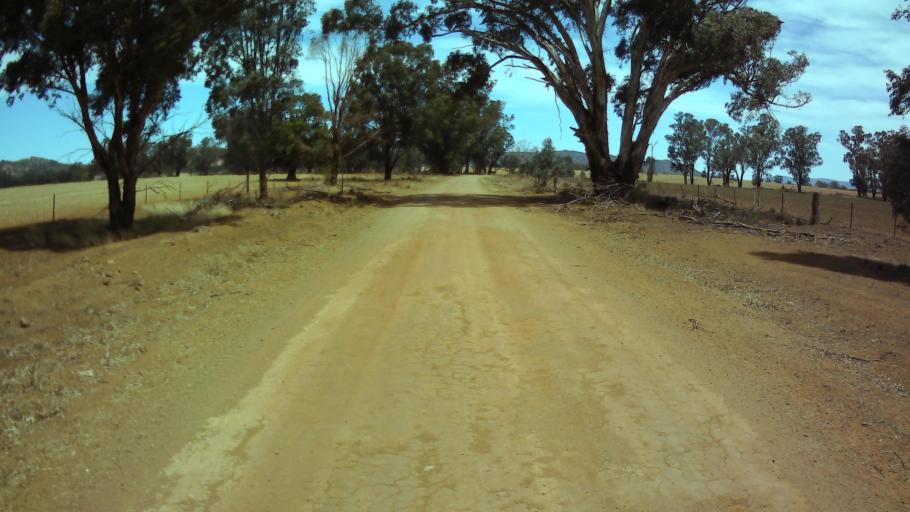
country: AU
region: New South Wales
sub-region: Weddin
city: Grenfell
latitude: -33.7560
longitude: 148.1435
